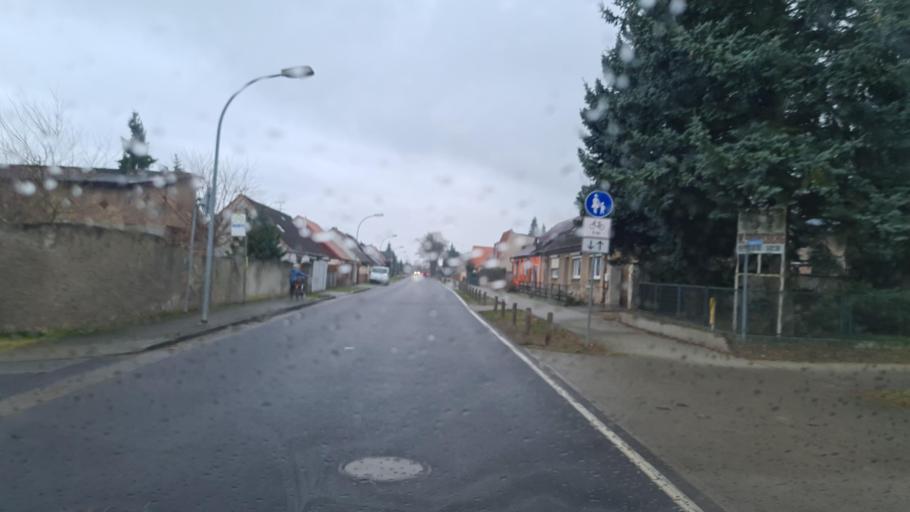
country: DE
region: Brandenburg
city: Zehdenick
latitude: 52.9085
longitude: 13.3025
